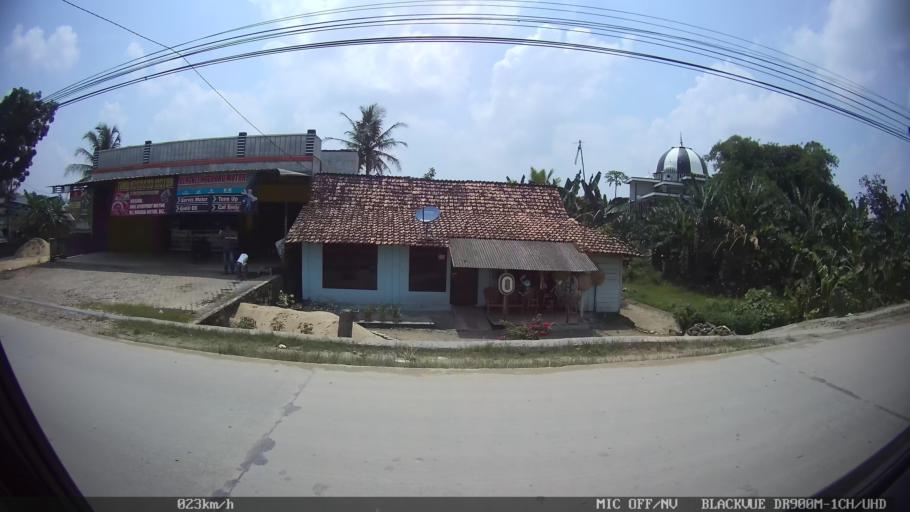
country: ID
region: Lampung
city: Pringsewu
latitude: -5.3424
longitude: 104.9747
